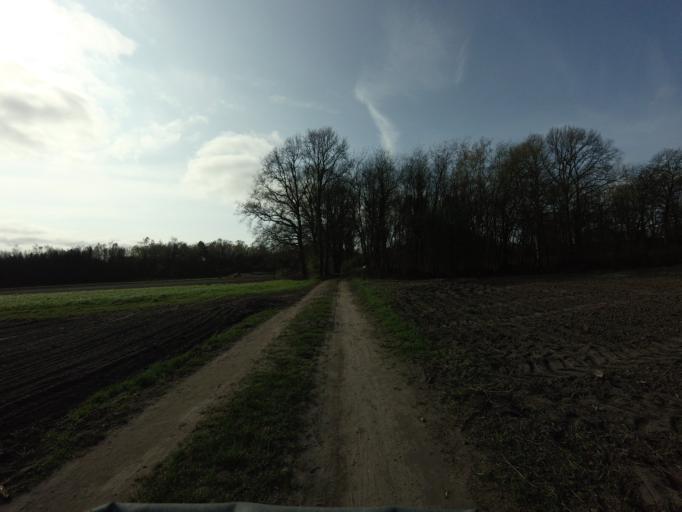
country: NL
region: North Holland
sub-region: Gemeente Laren
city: Laren
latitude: 52.2478
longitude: 5.2166
